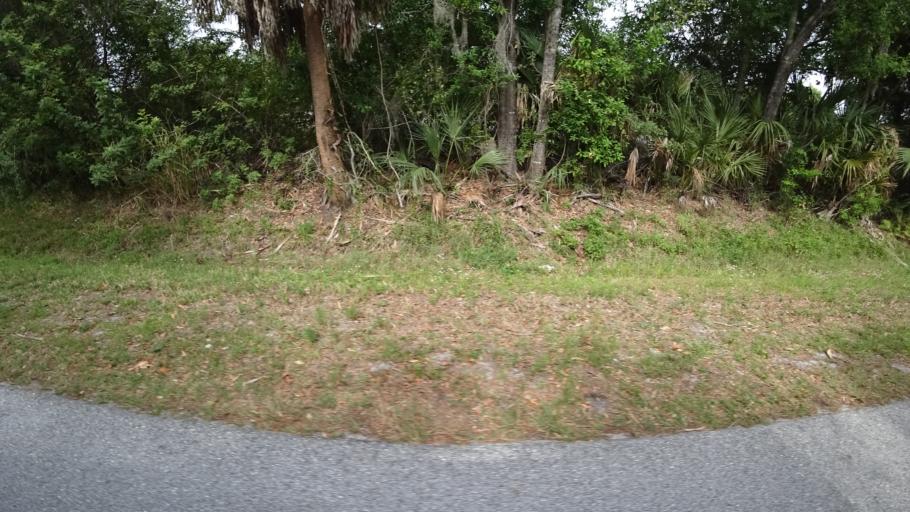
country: US
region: Florida
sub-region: Sarasota County
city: North Sarasota
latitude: 27.4026
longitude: -82.5301
